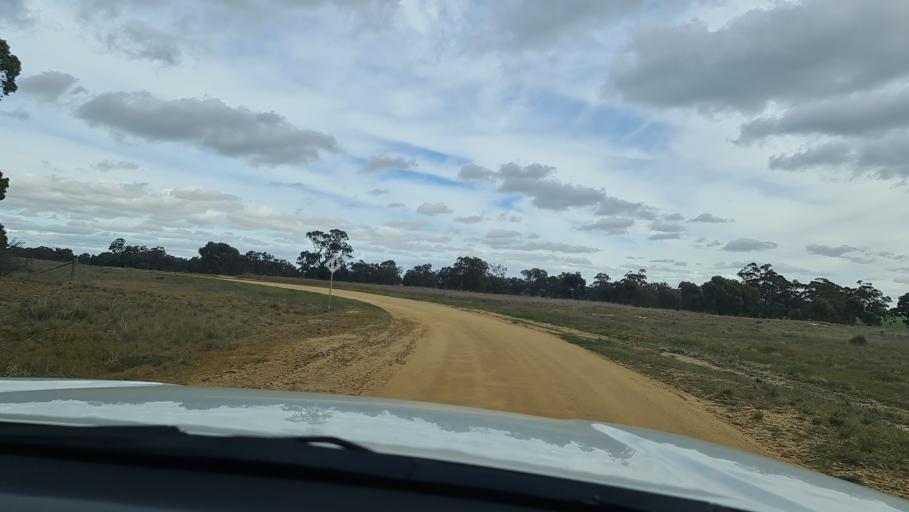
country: AU
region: Victoria
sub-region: Horsham
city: Horsham
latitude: -36.6202
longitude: 142.4208
